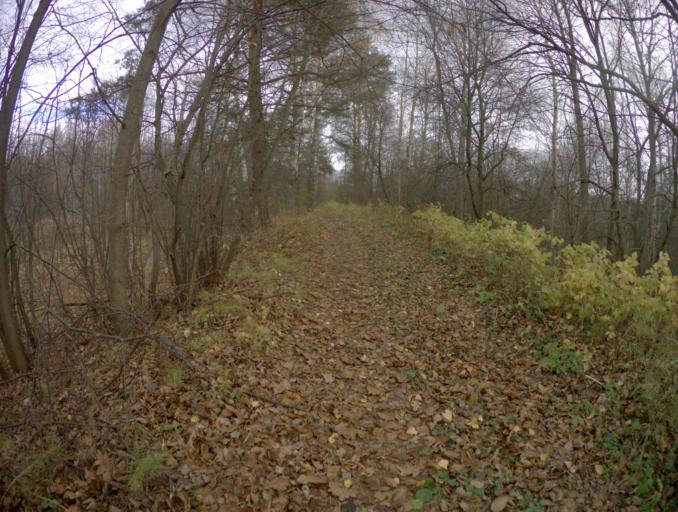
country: RU
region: Vladimir
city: Raduzhnyy
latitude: 56.0489
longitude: 40.3371
